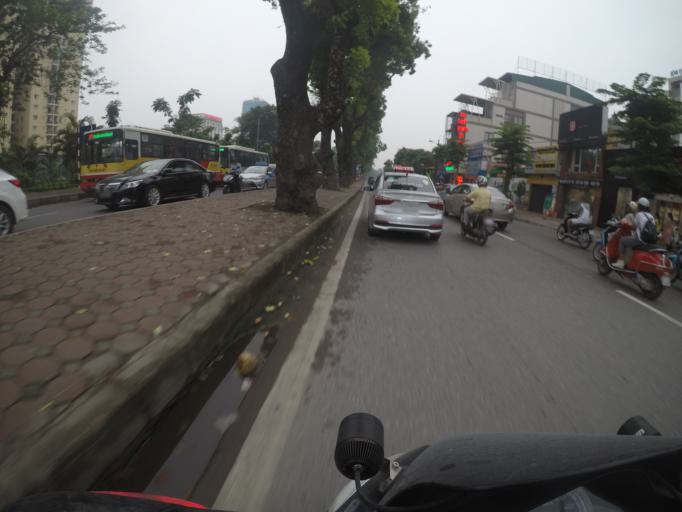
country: VN
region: Ha Noi
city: Thanh Xuan
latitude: 21.0113
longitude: 105.8106
